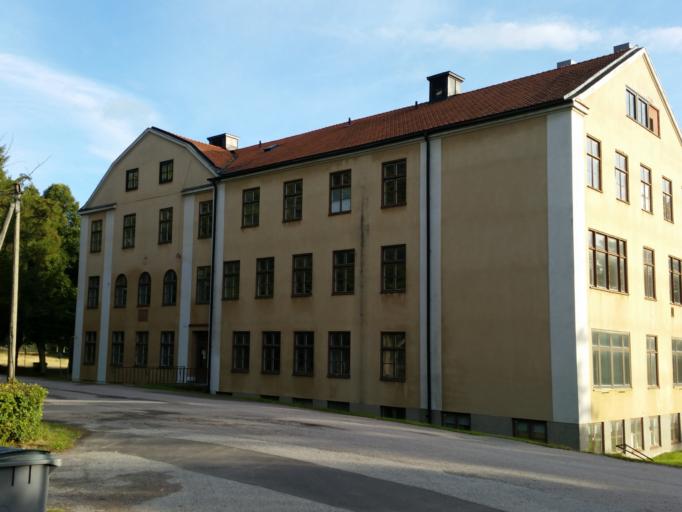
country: SE
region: Stockholm
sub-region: Upplands Vasby Kommun
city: Upplands Vaesby
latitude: 59.5406
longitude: 17.9139
